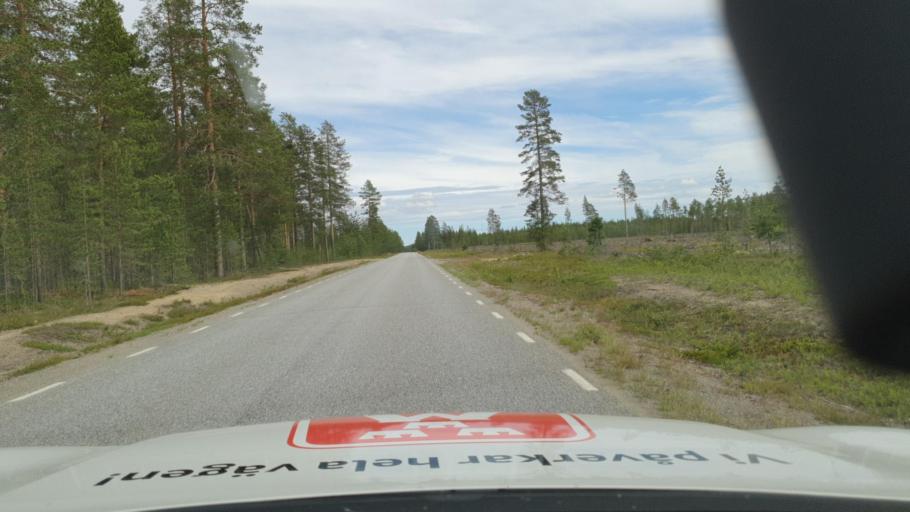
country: SE
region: Vaesterbotten
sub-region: Skelleftea Kommun
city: Burtraesk
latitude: 64.5052
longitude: 20.8047
